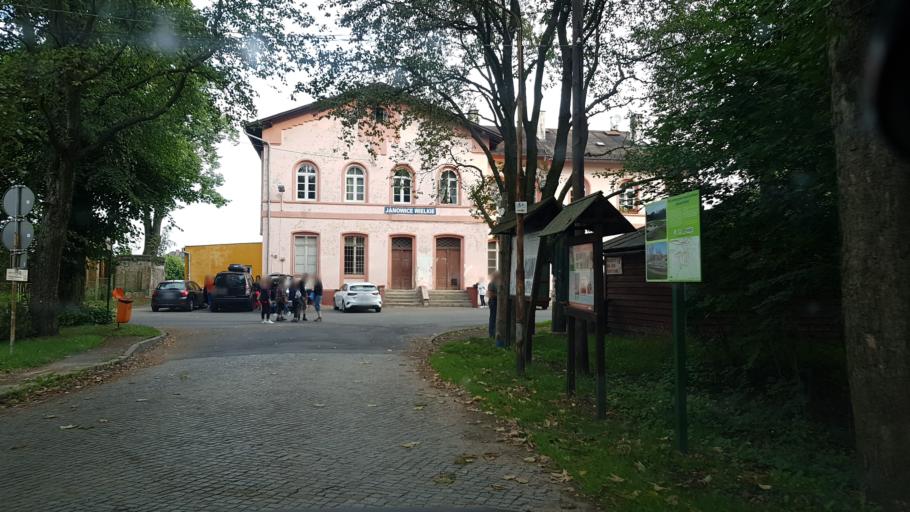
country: PL
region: Lower Silesian Voivodeship
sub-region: Powiat jeleniogorski
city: Janowice Wielkie
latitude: 50.8778
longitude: 15.9189
